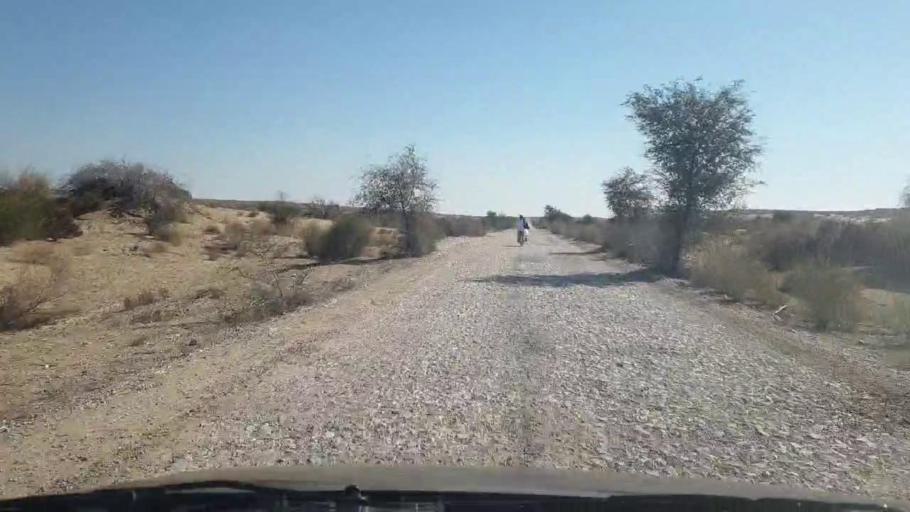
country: PK
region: Sindh
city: Bozdar
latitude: 27.0314
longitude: 68.7031
